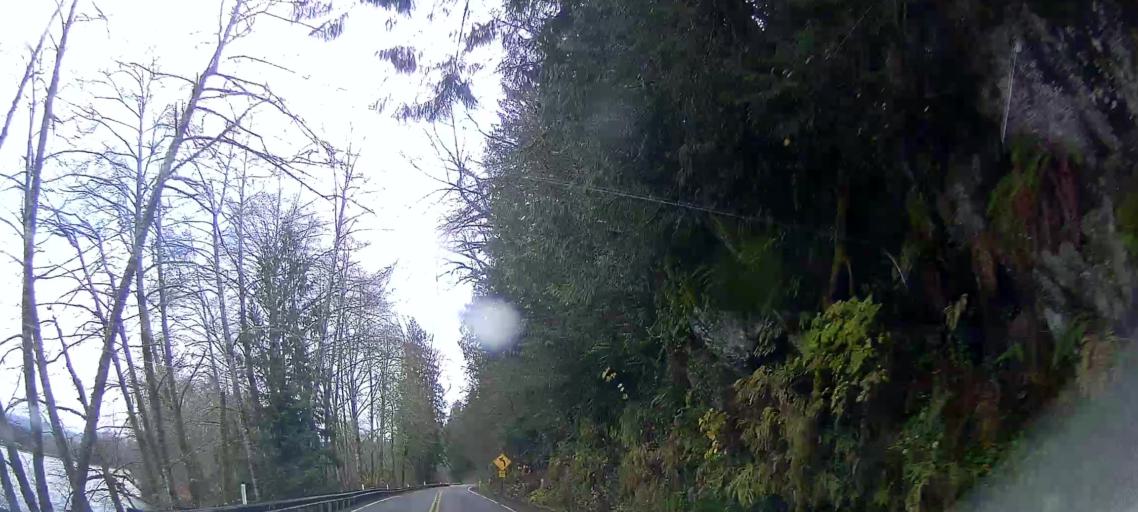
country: US
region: Washington
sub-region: Skagit County
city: Sedro-Woolley
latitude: 48.5151
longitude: -121.9760
